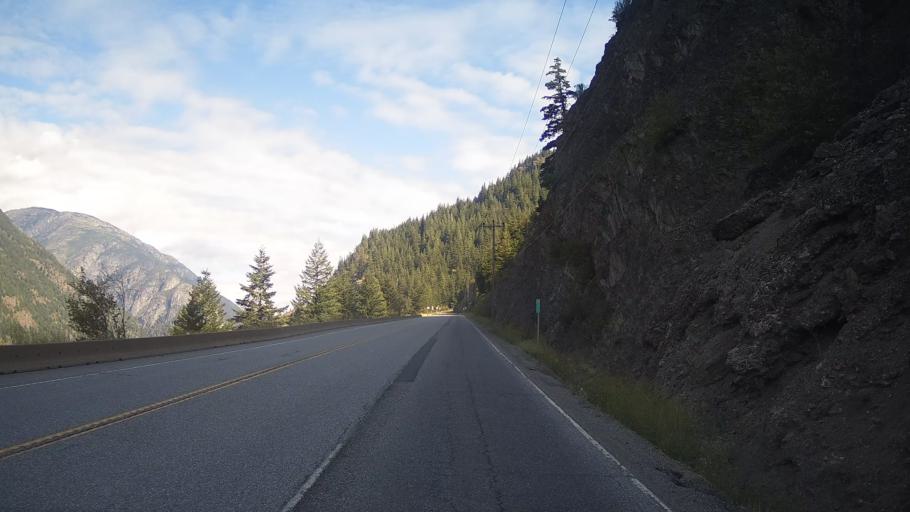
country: CA
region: British Columbia
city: Hope
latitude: 50.0690
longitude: -121.5456
